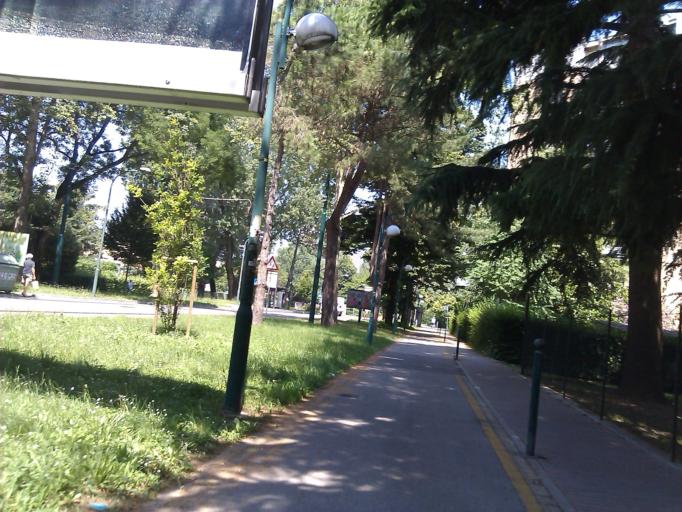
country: IT
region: Veneto
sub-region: Provincia di Venezia
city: Mestre
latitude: 45.4805
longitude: 12.2627
